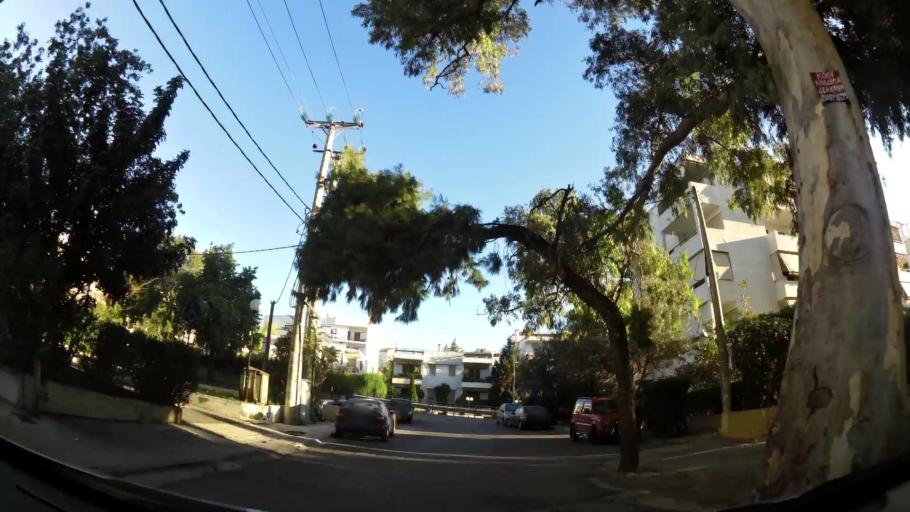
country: GR
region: Attica
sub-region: Nomarchia Athinas
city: Marousi
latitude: 38.0493
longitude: 23.7979
